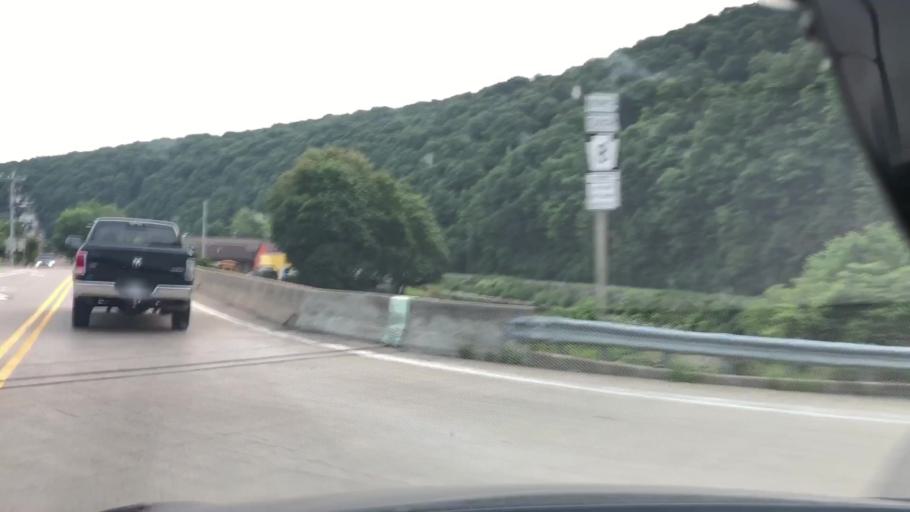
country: US
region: Pennsylvania
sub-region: Venango County
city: Oil City
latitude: 41.4431
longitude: -79.7063
